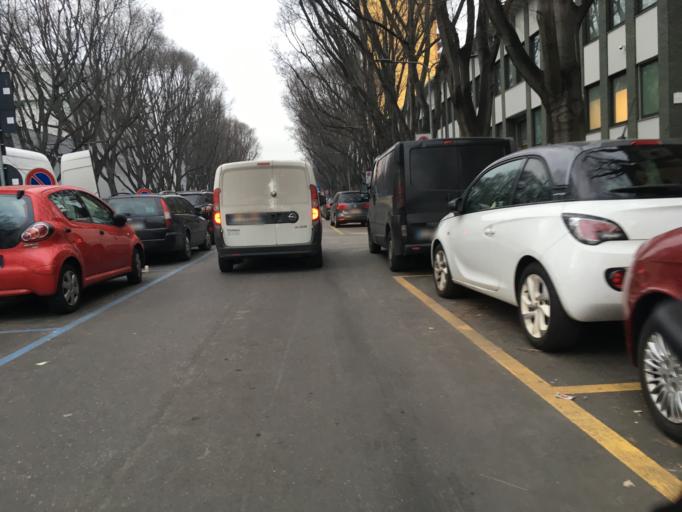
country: IT
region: Lombardy
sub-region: Citta metropolitana di Milano
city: Milano
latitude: 45.4509
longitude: 9.1657
